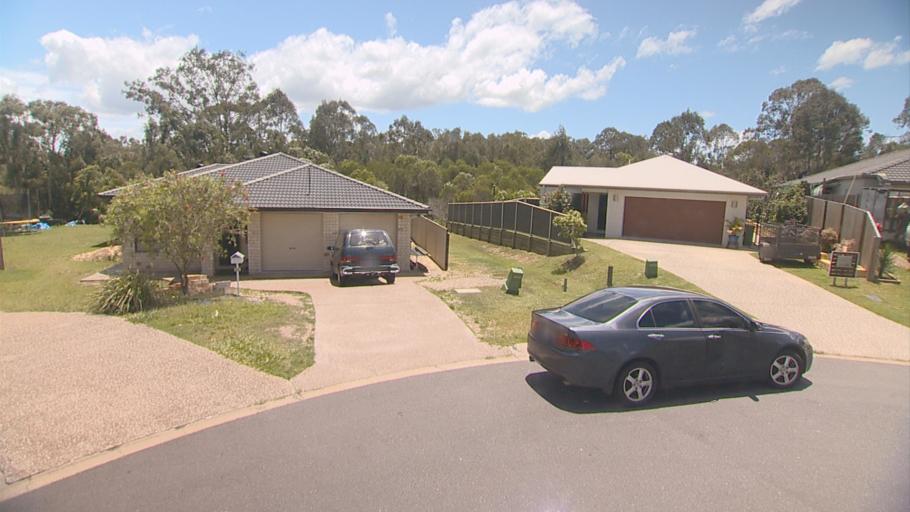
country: AU
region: Queensland
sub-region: Logan
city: Beenleigh
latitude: -27.6955
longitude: 153.2023
